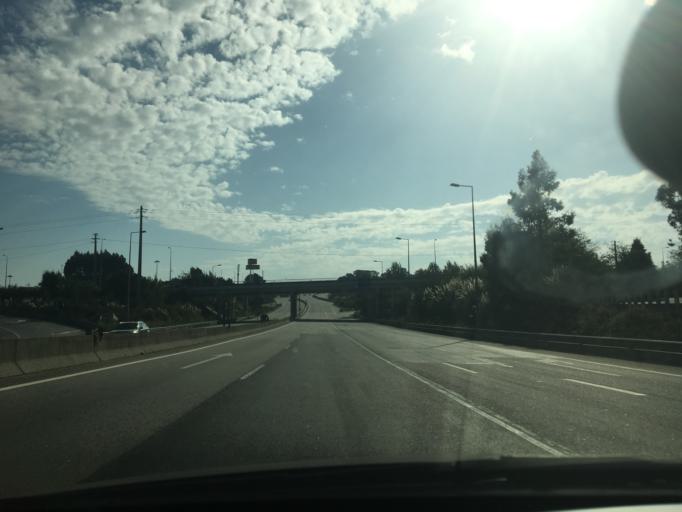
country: PT
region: Porto
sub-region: Maia
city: Leca do Bailio
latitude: 41.2043
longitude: -8.6275
